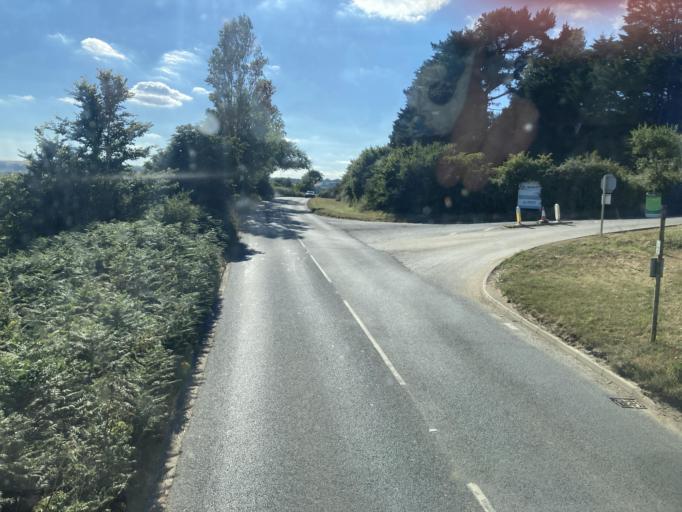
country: GB
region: England
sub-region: Isle of Wight
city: Newport
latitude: 50.6720
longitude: -1.2729
